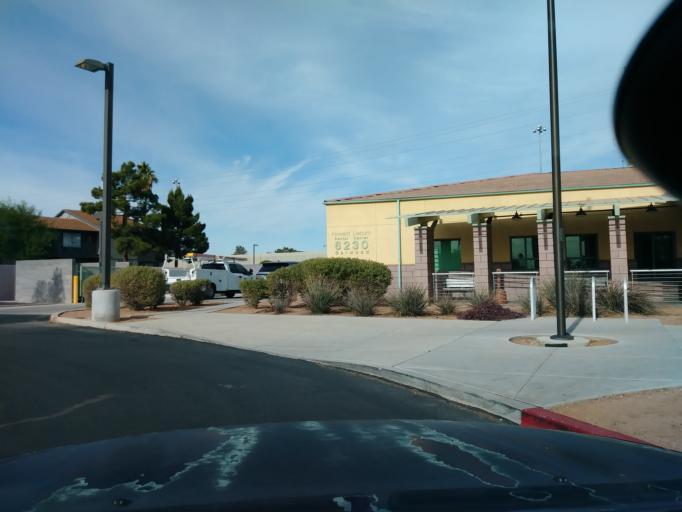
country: US
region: Nevada
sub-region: Clark County
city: Spring Valley
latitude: 36.1731
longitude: -115.2285
